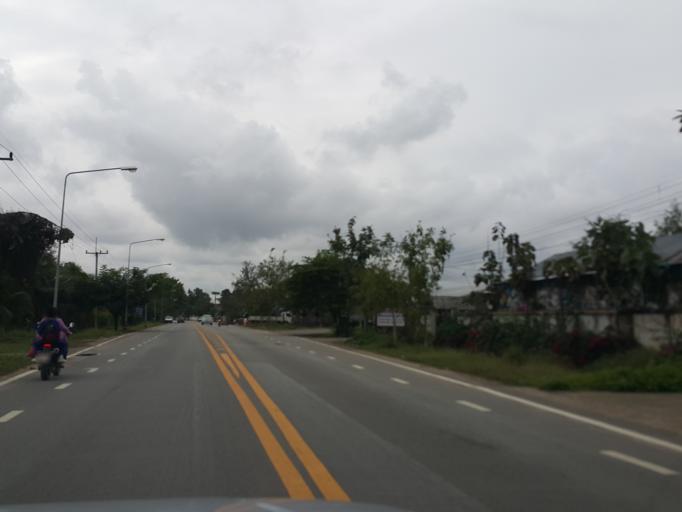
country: TH
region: Lamphun
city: Ban Thi
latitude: 18.5969
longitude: 99.0831
